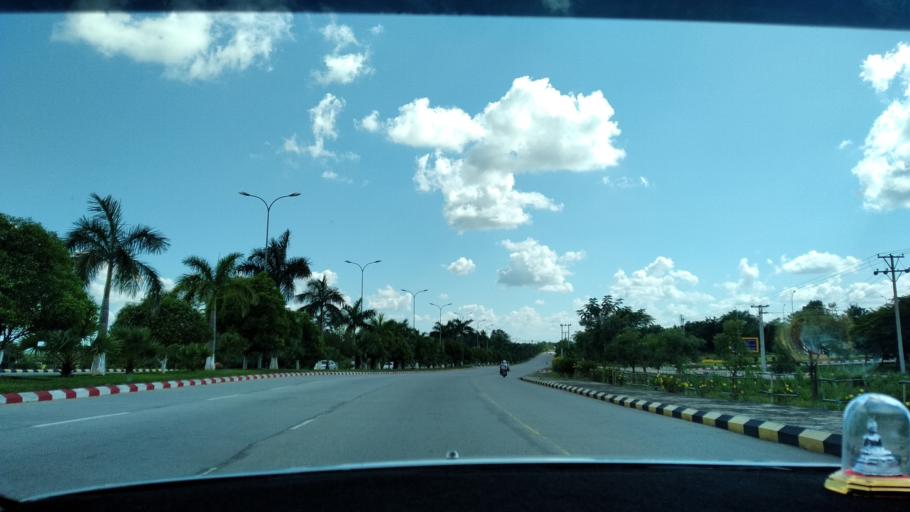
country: MM
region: Mandalay
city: Nay Pyi Taw
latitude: 19.7761
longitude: 96.1430
